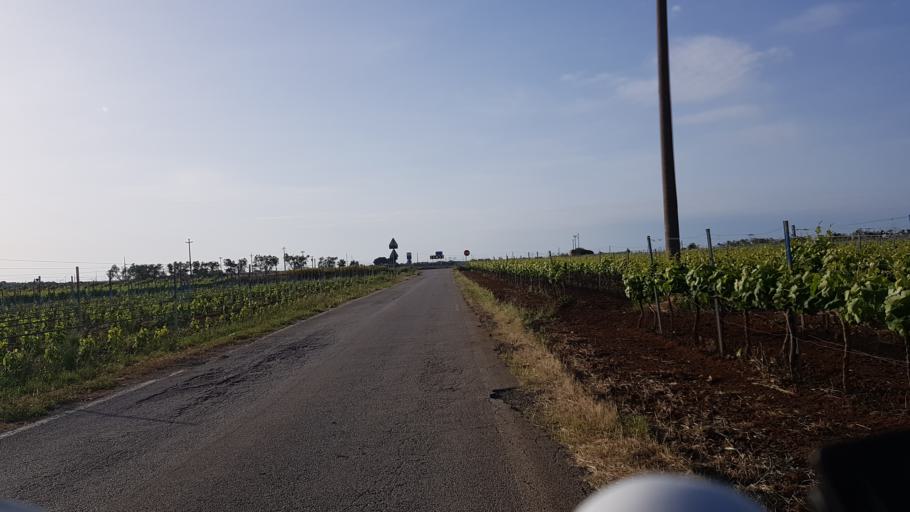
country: IT
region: Apulia
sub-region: Provincia di Brindisi
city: Mesagne
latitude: 40.5878
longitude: 17.8568
